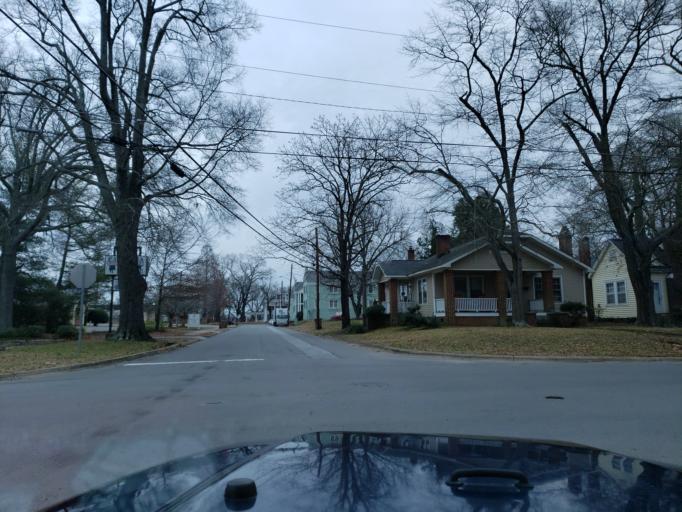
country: US
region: North Carolina
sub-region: Cleveland County
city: Shelby
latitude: 35.3003
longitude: -81.5416
